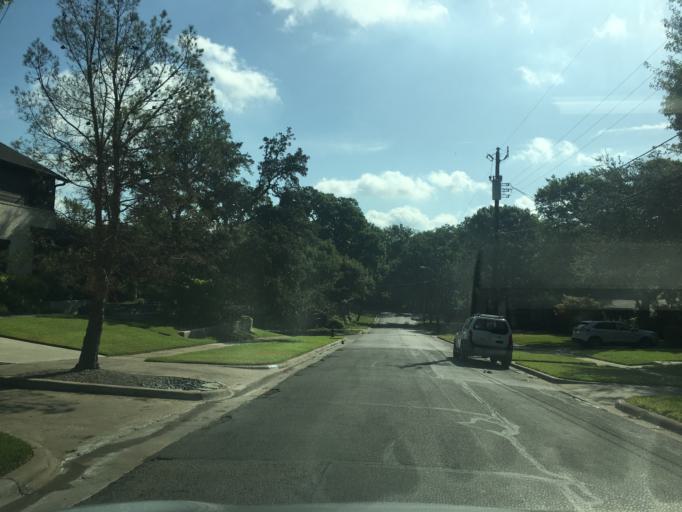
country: US
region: Texas
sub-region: Dallas County
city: Highland Park
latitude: 32.8329
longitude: -96.7398
